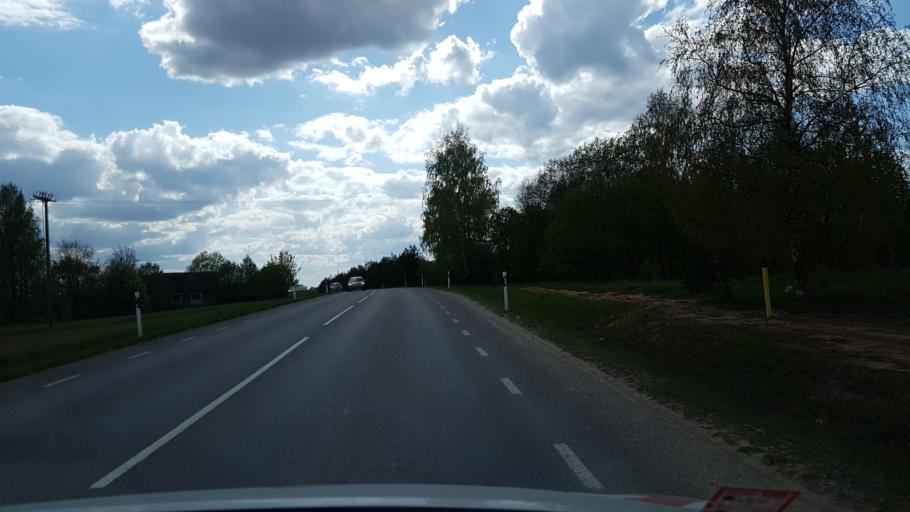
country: EE
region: Tartu
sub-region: Tartu linn
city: Tartu
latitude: 58.3916
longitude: 26.8130
